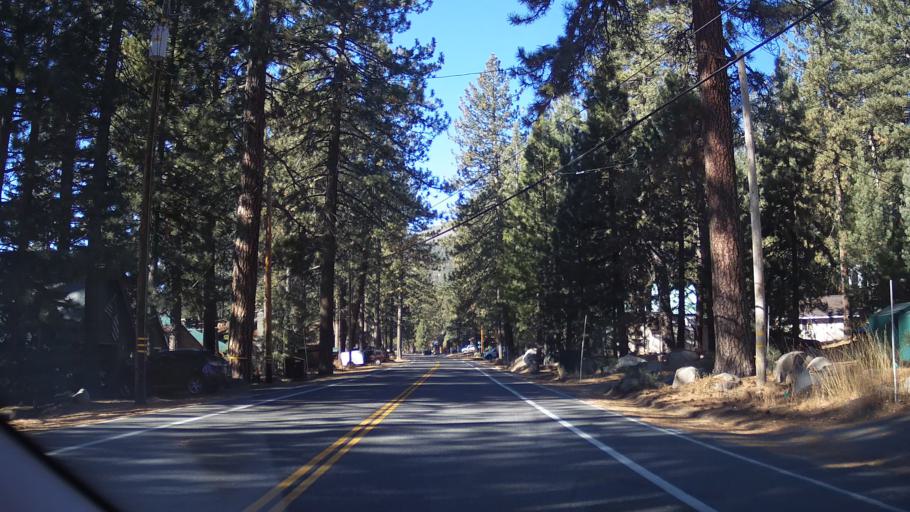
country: US
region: California
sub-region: Nevada County
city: Truckee
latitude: 39.3283
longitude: -120.2467
